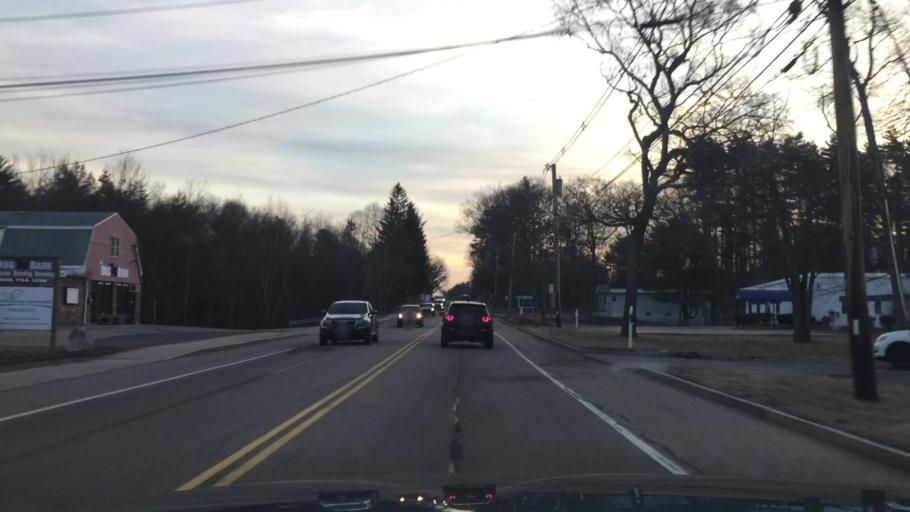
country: US
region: Massachusetts
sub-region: Norfolk County
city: Millis
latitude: 42.1598
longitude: -71.3799
